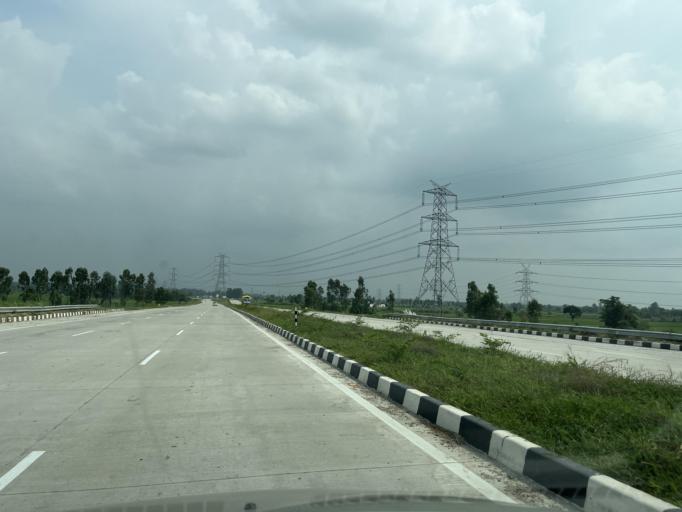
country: IN
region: Uttarakhand
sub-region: Udham Singh Nagar
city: Jaspur
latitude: 29.2876
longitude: 78.8547
